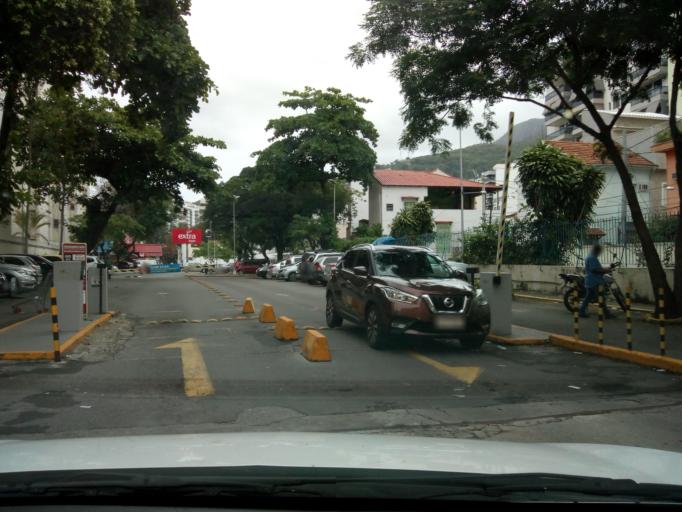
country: BR
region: Rio de Janeiro
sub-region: Rio De Janeiro
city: Rio de Janeiro
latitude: -22.9174
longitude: -43.2233
